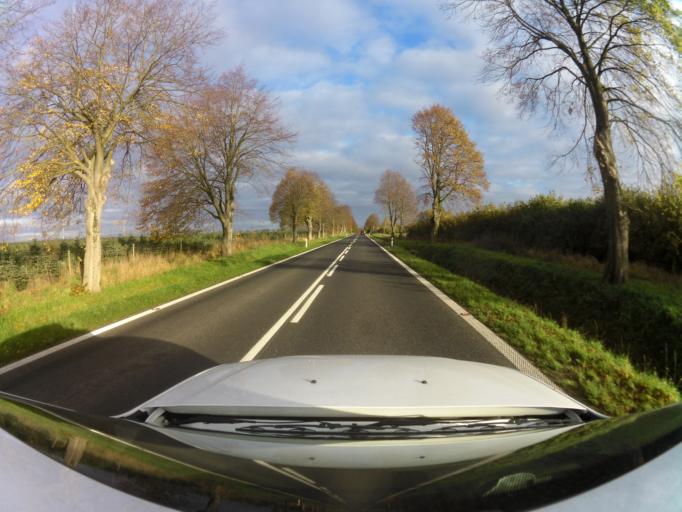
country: PL
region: West Pomeranian Voivodeship
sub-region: Powiat gryficki
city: Trzebiatow
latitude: 54.0001
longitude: 15.2395
